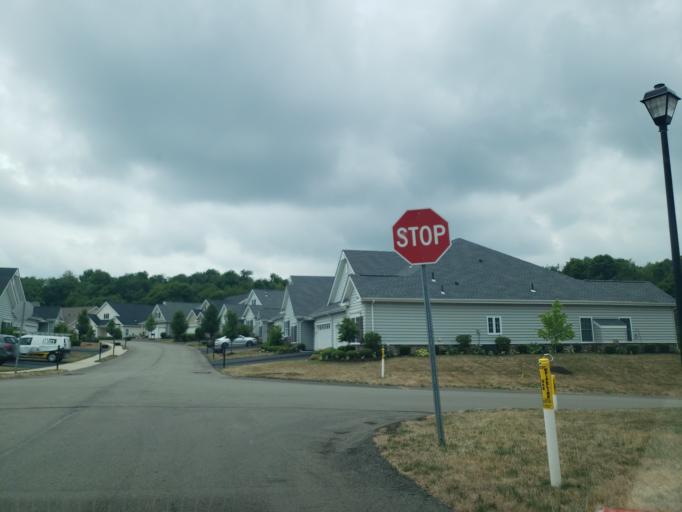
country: US
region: Pennsylvania
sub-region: Allegheny County
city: Emsworth
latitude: 40.5374
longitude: -80.1202
